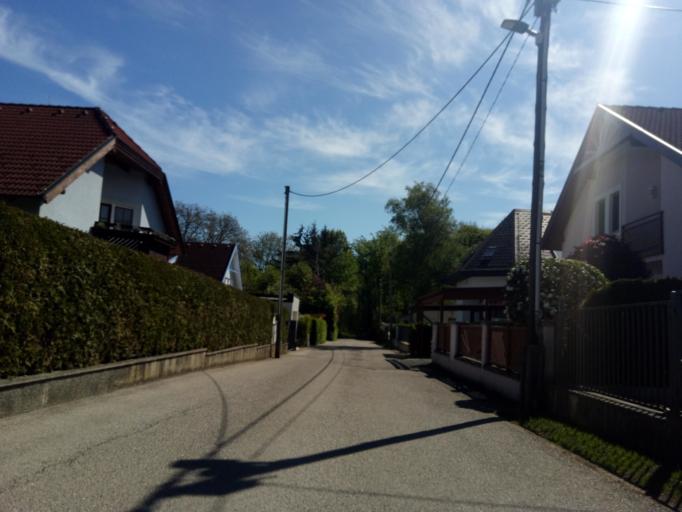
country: AT
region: Lower Austria
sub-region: Politischer Bezirk Modling
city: Kaltenleutgeben
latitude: 48.1349
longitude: 16.2030
